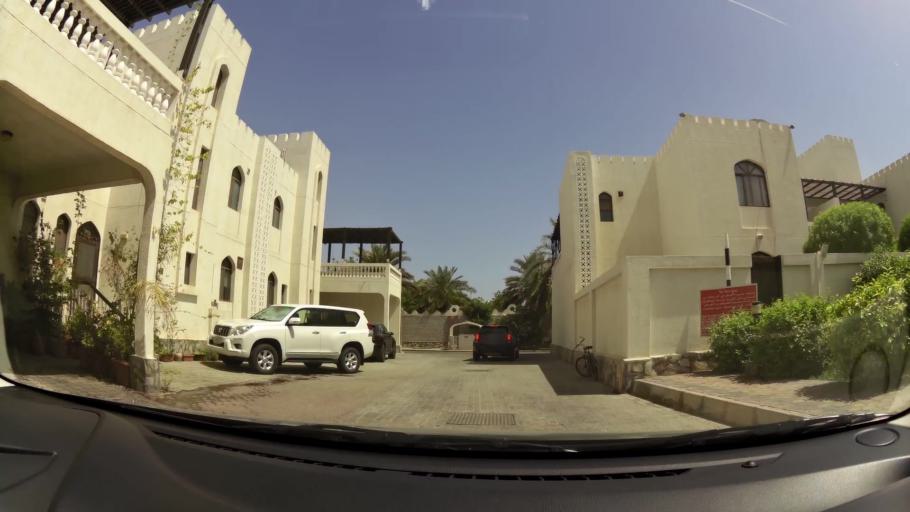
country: OM
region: Muhafazat Masqat
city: Bawshar
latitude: 23.5967
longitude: 58.4511
